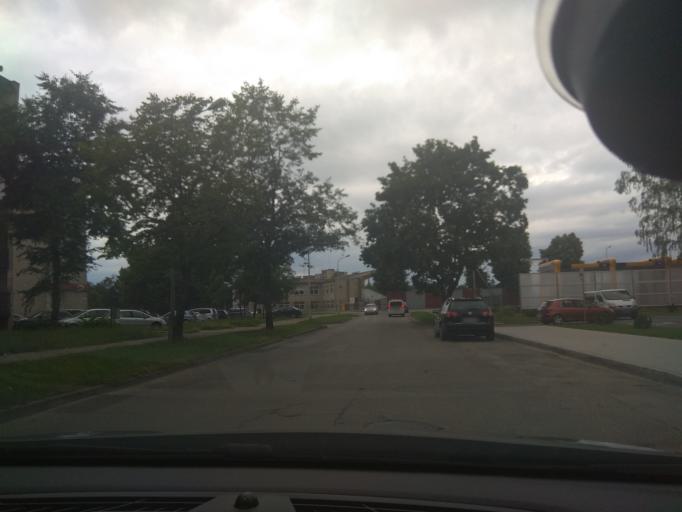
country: LT
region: Marijampoles apskritis
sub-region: Marijampole Municipality
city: Marijampole
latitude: 54.5671
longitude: 23.3625
